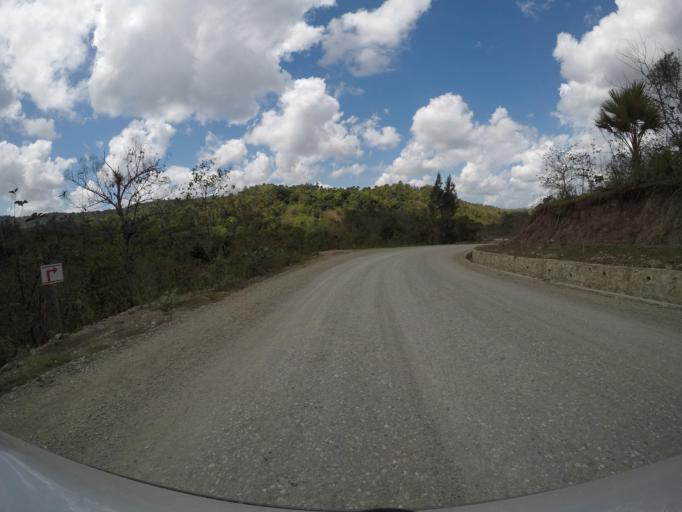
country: TL
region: Viqueque
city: Viqueque
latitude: -8.8117
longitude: 126.3816
